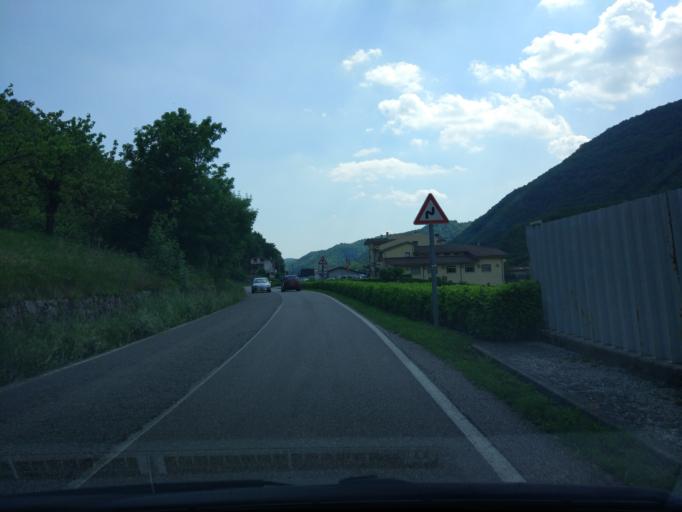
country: IT
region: Veneto
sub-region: Provincia di Verona
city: Badia Calavena
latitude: 45.5862
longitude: 11.1538
